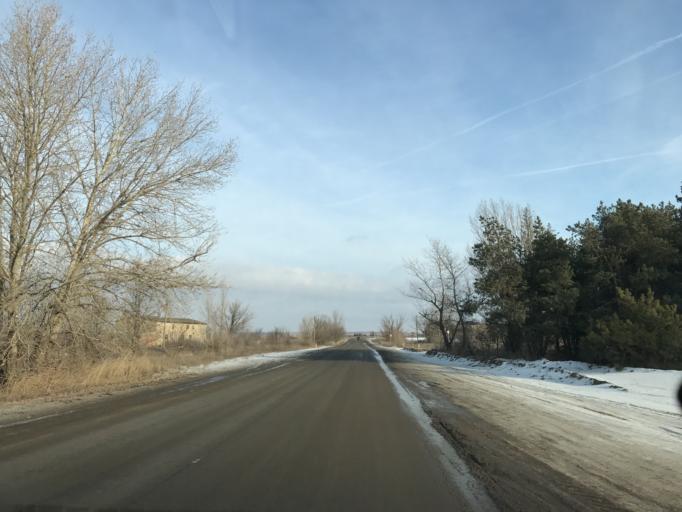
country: RU
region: Rostov
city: Staraya Stanitsa
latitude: 48.2383
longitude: 40.4055
